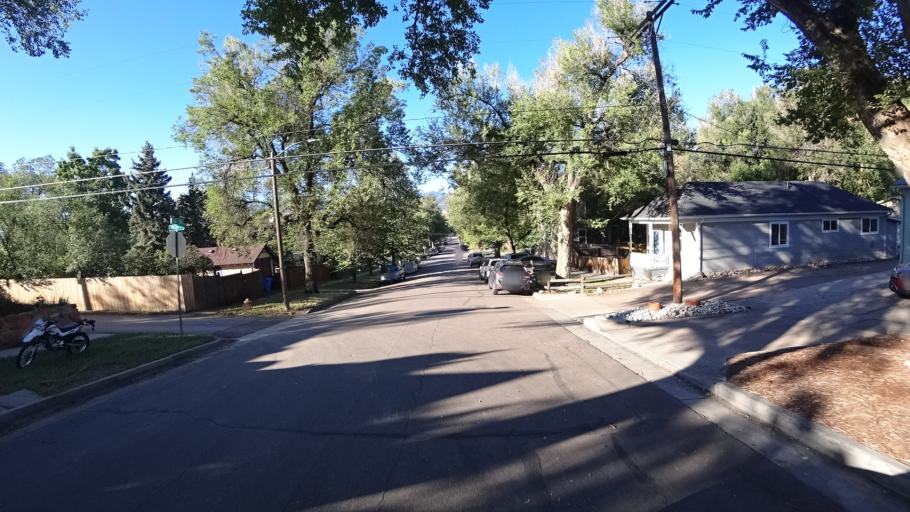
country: US
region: Colorado
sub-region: El Paso County
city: Colorado Springs
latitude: 38.8396
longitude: -104.8435
